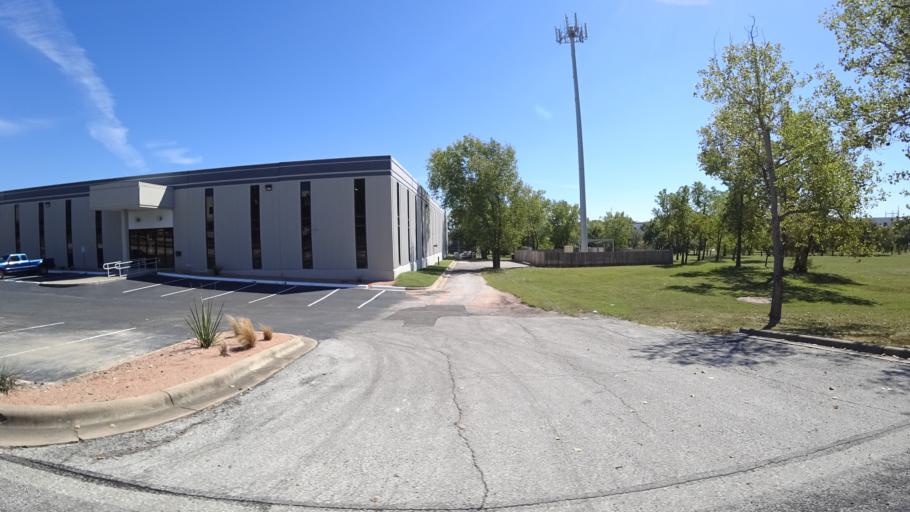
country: US
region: Texas
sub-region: Travis County
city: Austin
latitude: 30.2156
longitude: -97.6923
